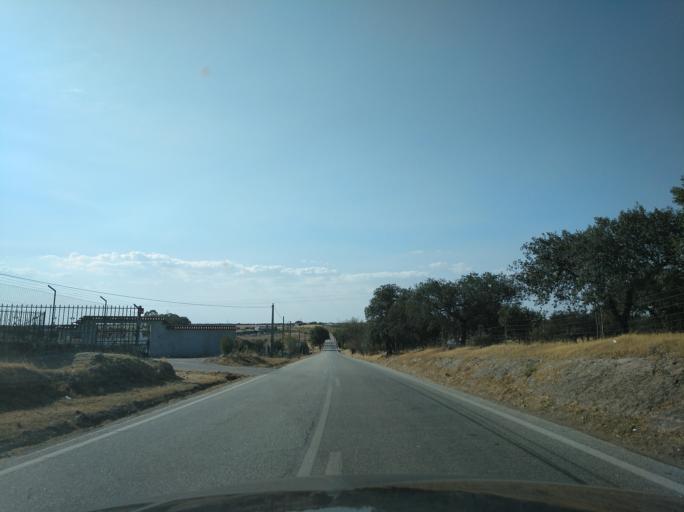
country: ES
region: Extremadura
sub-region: Provincia de Badajoz
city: Valencia del Mombuey
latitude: 38.2235
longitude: -7.2250
